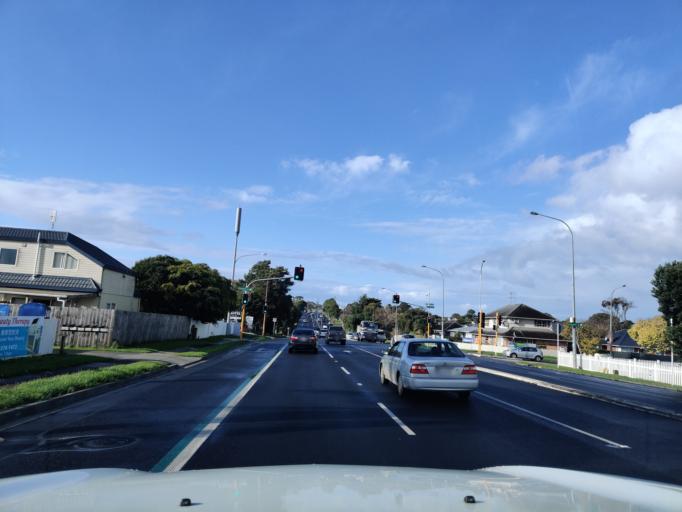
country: NZ
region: Auckland
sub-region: Auckland
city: Tamaki
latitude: -36.9063
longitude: 174.8886
